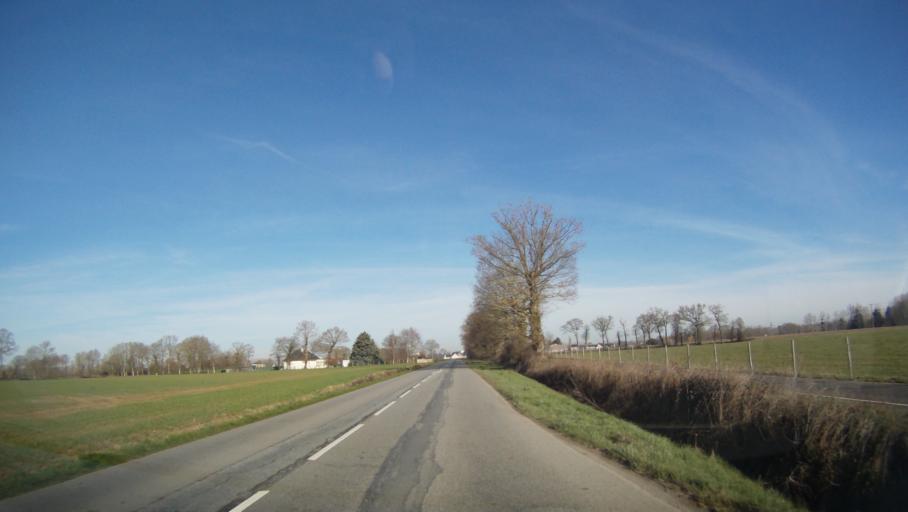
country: FR
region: Brittany
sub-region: Departement d'Ille-et-Vilaine
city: Chatillon-sur-Seiche
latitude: 48.0291
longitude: -1.6599
